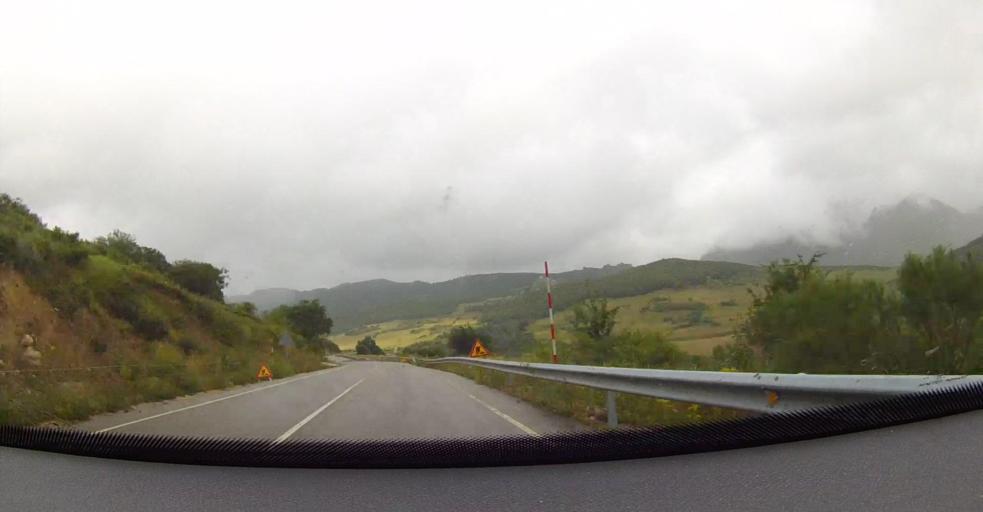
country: ES
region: Castille and Leon
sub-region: Provincia de Leon
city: Marana
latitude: 43.0724
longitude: -5.2049
